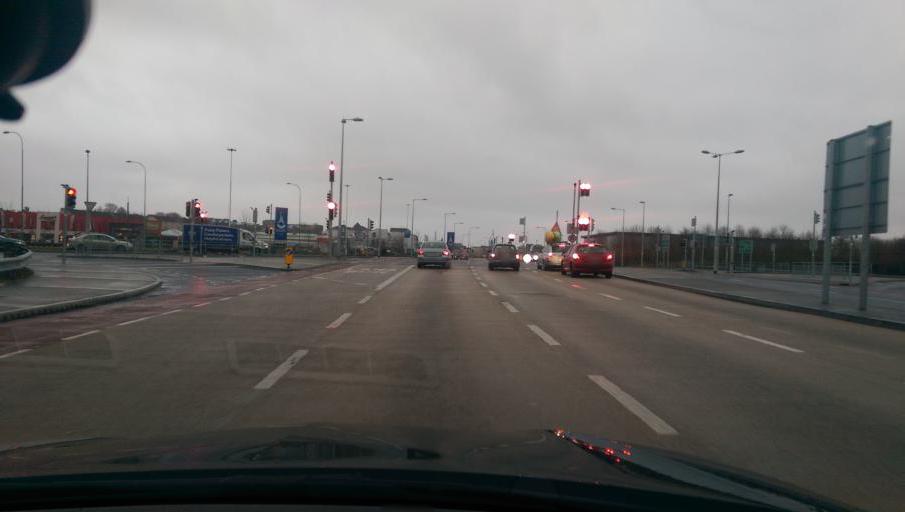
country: IE
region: Connaught
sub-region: County Galway
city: Gaillimh
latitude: 53.2827
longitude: -9.0475
